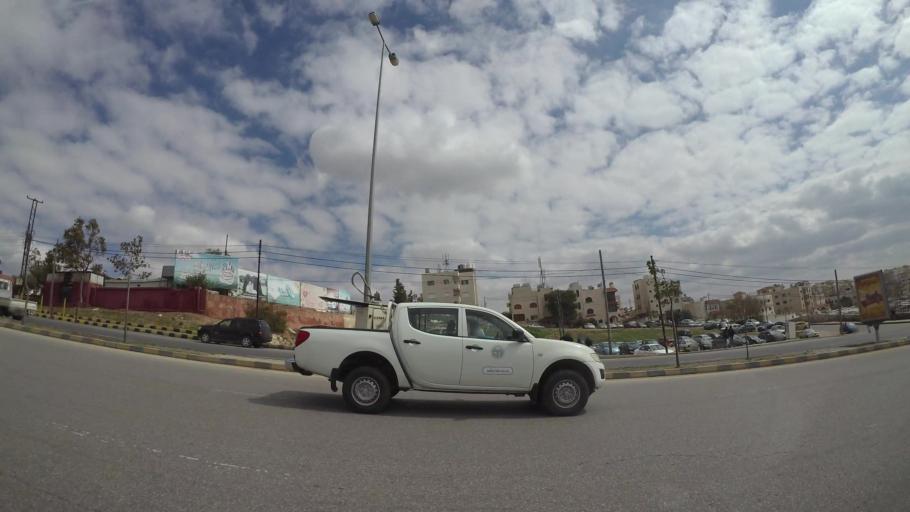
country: JO
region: Amman
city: Amman
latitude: 31.9963
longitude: 35.9184
